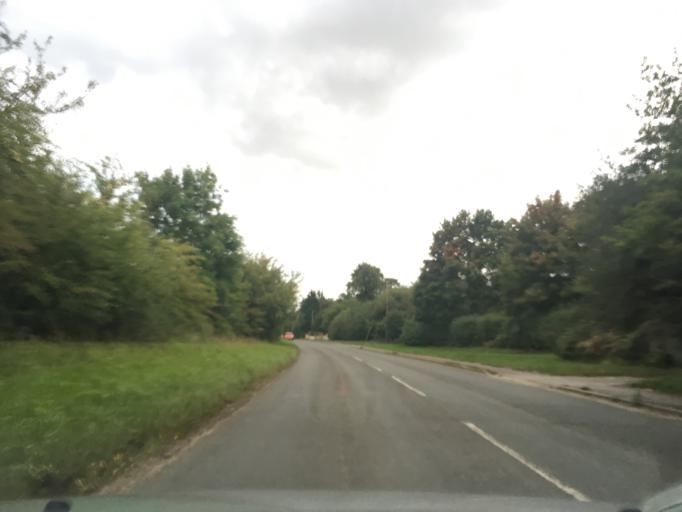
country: GB
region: England
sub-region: Oxfordshire
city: Cowley
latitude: 51.7770
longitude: -1.1881
